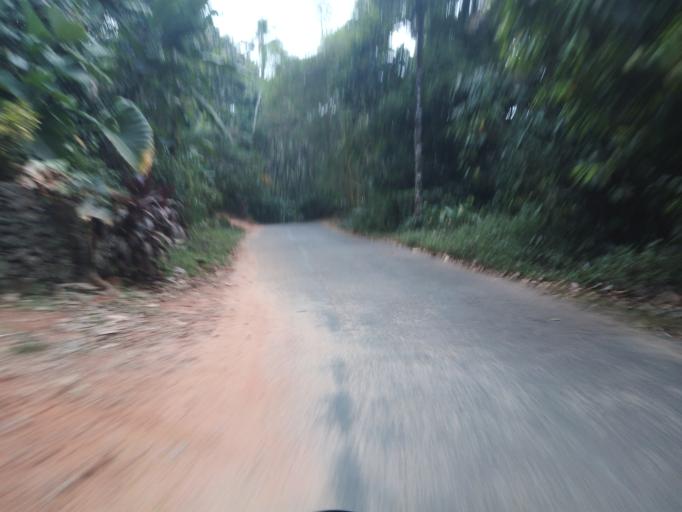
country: IN
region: Kerala
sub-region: Ernakulam
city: Muvattupuzha
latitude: 9.8743
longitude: 76.6495
